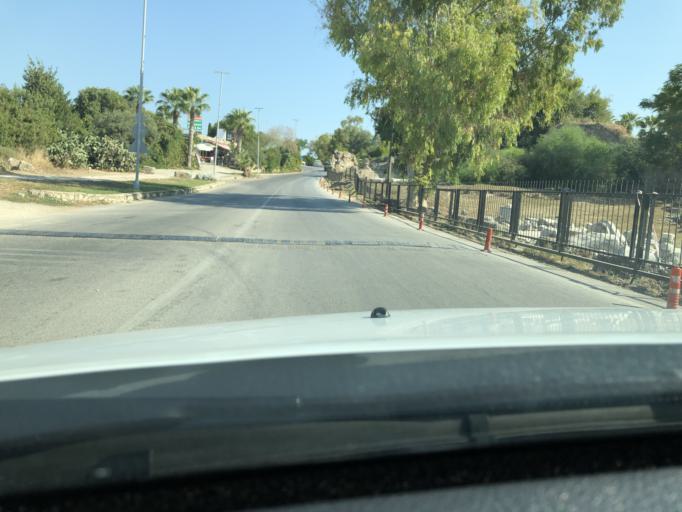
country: TR
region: Antalya
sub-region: Manavgat
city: Side
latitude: 36.7712
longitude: 31.3945
